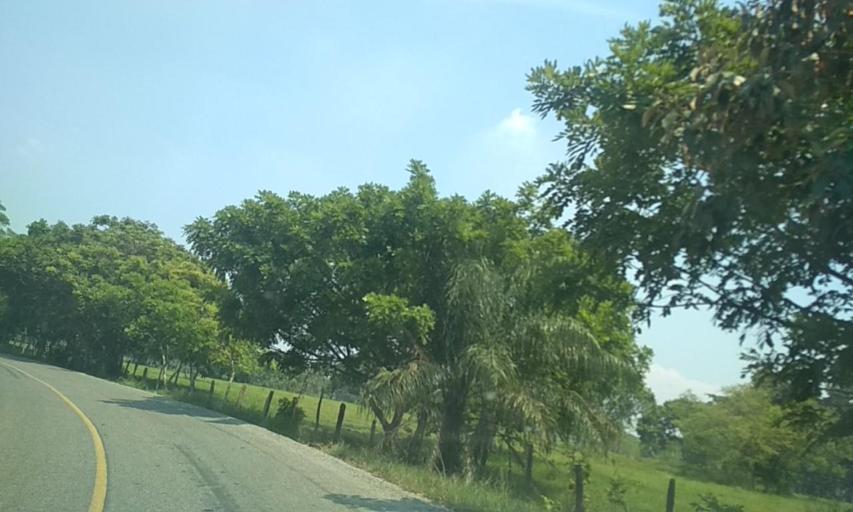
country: MX
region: Tabasco
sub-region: Huimanguillo
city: C-41 (Licenciado Carlos A. Madrazo)
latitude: 17.8299
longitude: -93.5128
